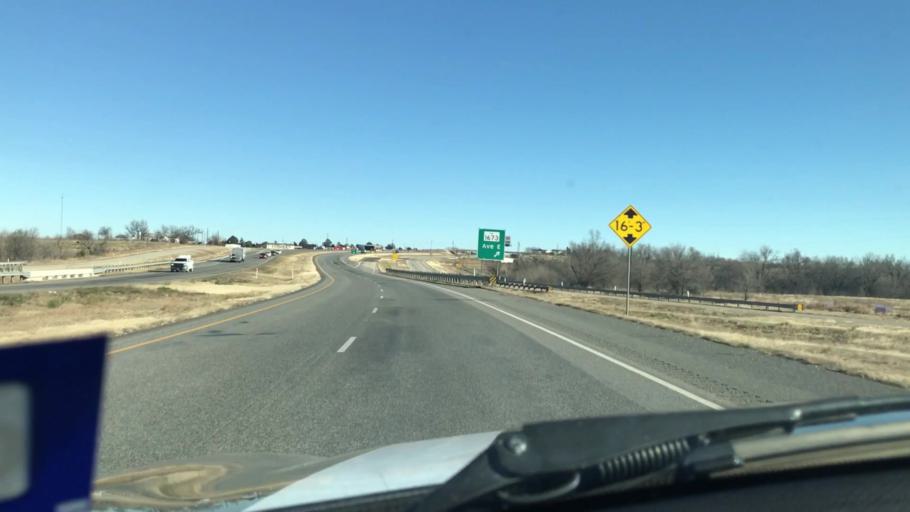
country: US
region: Texas
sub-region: Scurry County
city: Snyder
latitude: 32.7342
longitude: -100.9106
